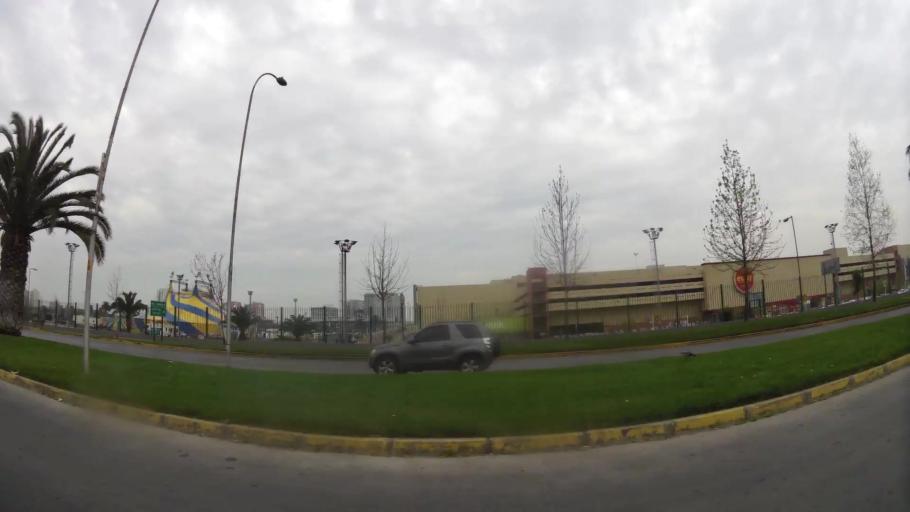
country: CL
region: Santiago Metropolitan
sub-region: Provincia de Santiago
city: Villa Presidente Frei, Nunoa, Santiago, Chile
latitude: -33.5101
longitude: -70.6040
